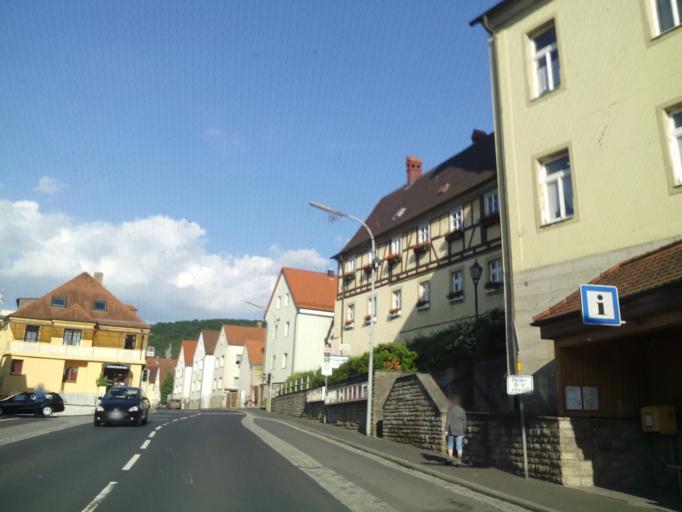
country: DE
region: Bavaria
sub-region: Regierungsbezirk Unterfranken
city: Nudlingen
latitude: 50.2211
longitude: 10.1239
